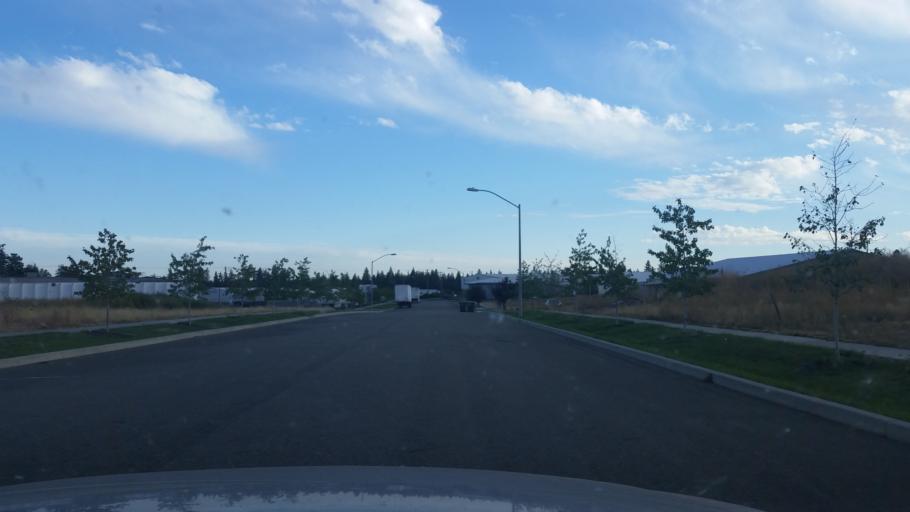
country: US
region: Washington
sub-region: Spokane County
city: Cheney
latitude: 47.4758
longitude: -117.6052
